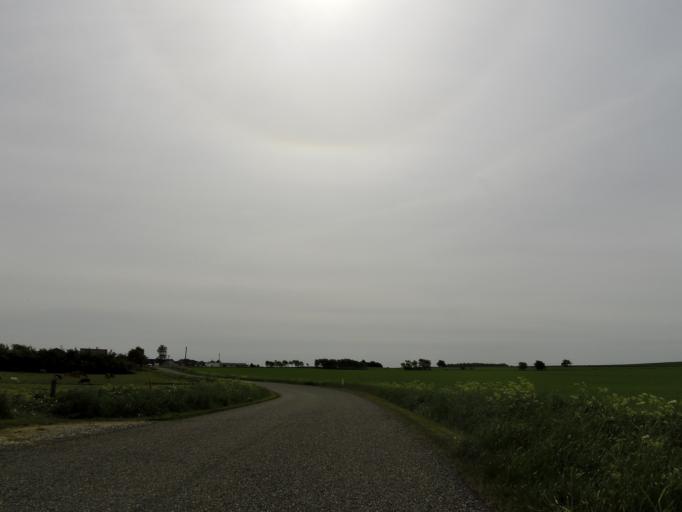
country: DK
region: Central Jutland
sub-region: Holstebro Kommune
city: Vinderup
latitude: 56.5853
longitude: 8.7743
